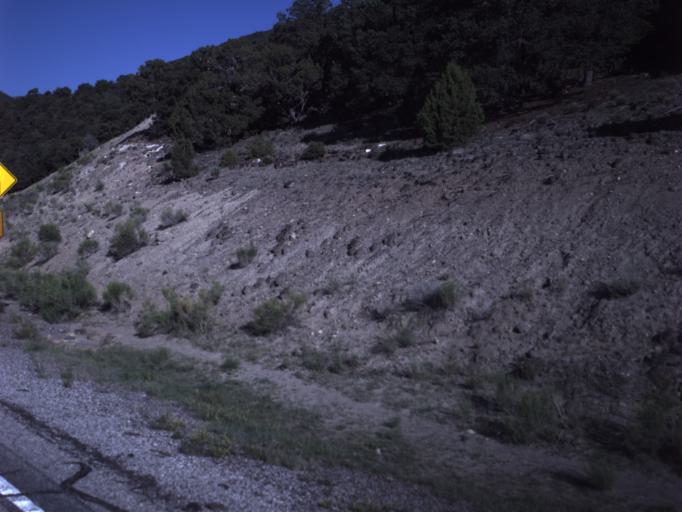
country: US
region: Utah
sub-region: Wayne County
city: Loa
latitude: 38.6758
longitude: -111.4027
